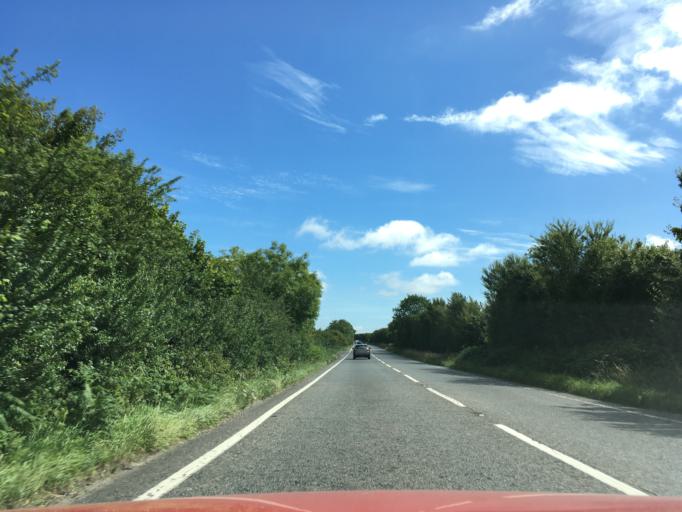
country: GB
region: England
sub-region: Dorset
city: Sherborne
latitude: 50.8175
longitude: -2.5564
